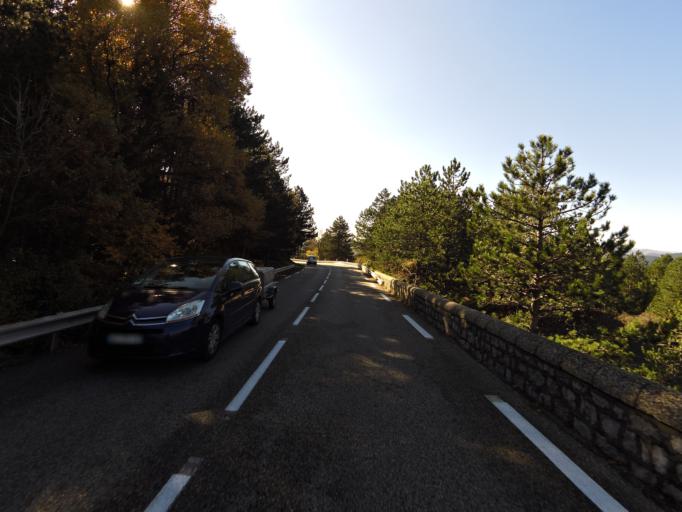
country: FR
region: Rhone-Alpes
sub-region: Departement de l'Ardeche
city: Vesseaux
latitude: 44.6976
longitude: 4.4788
